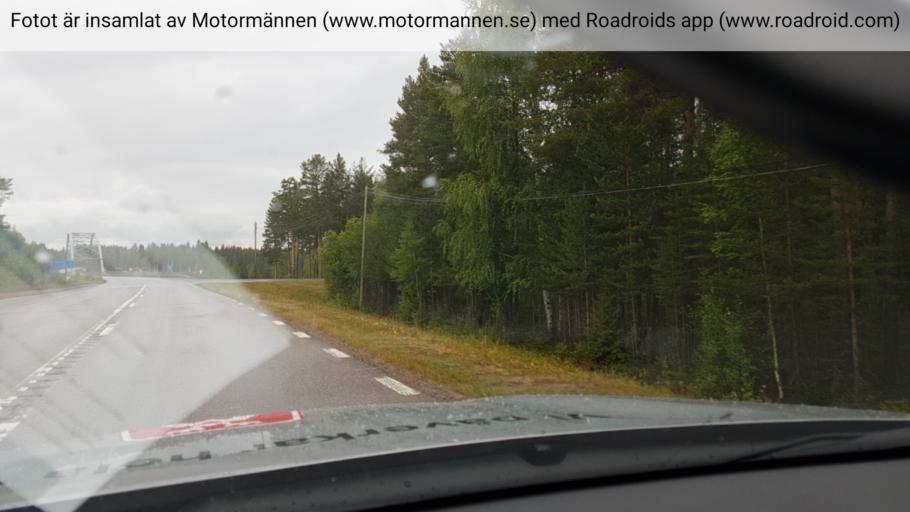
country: SE
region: Norrbotten
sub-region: Alvsbyns Kommun
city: AElvsbyn
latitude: 66.2291
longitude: 20.8741
